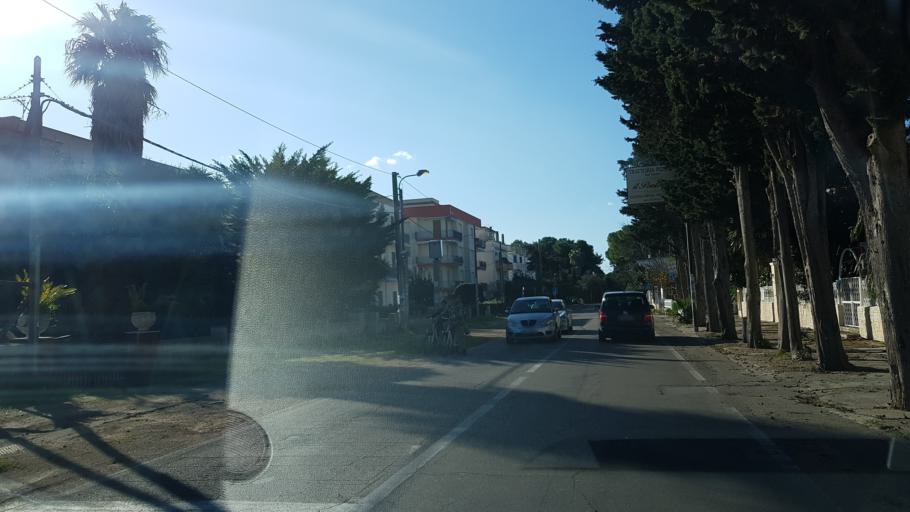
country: IT
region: Apulia
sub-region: Provincia di Lecce
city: Gallipoli
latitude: 40.0851
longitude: 18.0132
